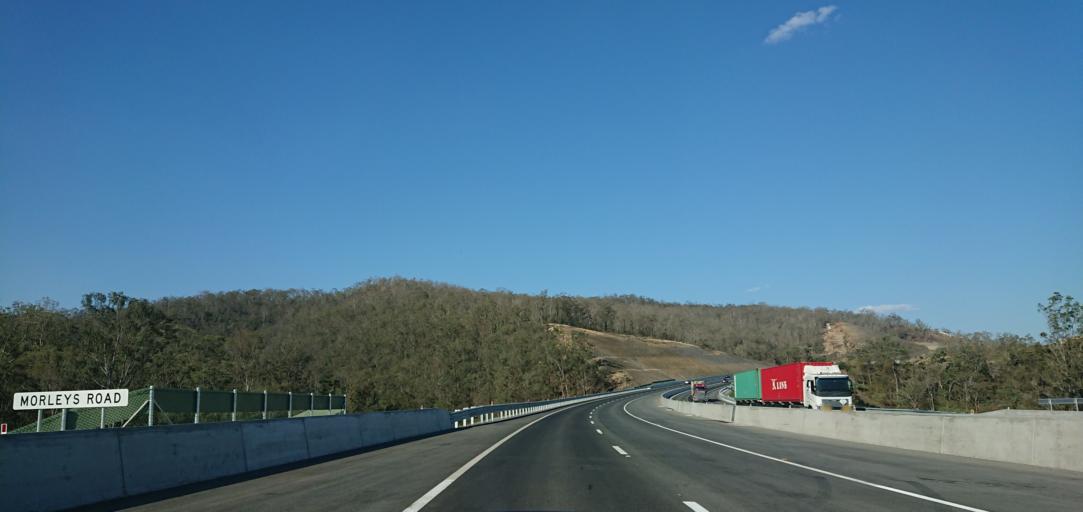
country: AU
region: Queensland
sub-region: Toowoomba
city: Wilsonton Heights
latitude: -27.4986
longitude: 151.9786
